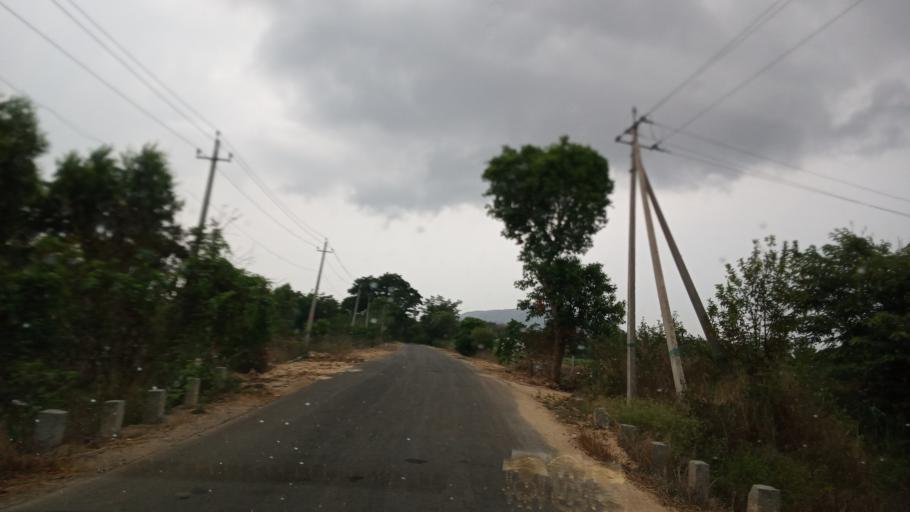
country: IN
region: Karnataka
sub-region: Kolar
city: Mulbagal
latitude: 13.1203
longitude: 78.3412
